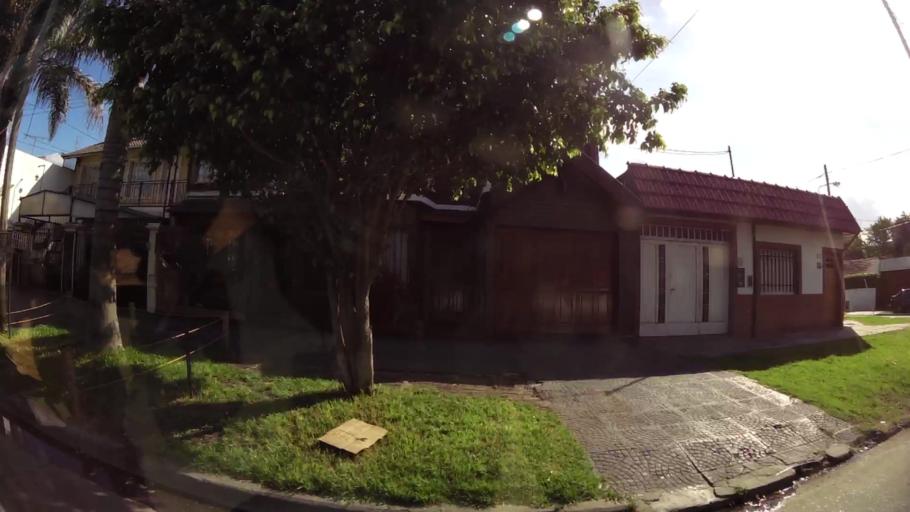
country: AR
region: Buenos Aires
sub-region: Partido de Moron
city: Moron
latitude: -34.6637
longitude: -58.5897
